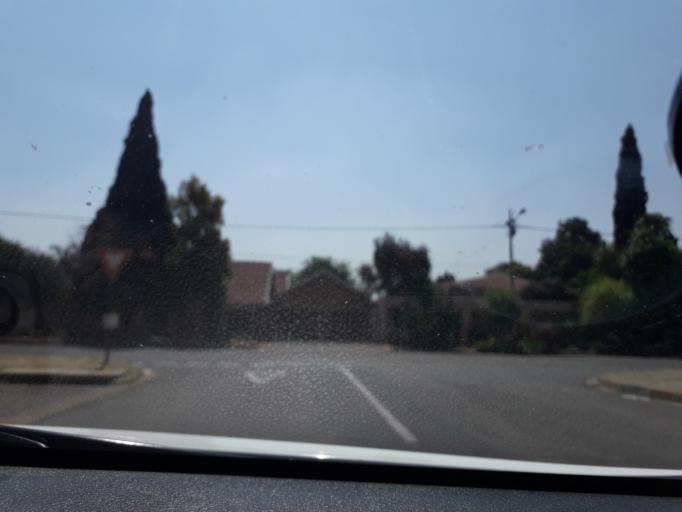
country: ZA
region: Gauteng
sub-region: City of Johannesburg Metropolitan Municipality
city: Modderfontein
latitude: -26.0920
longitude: 28.2245
